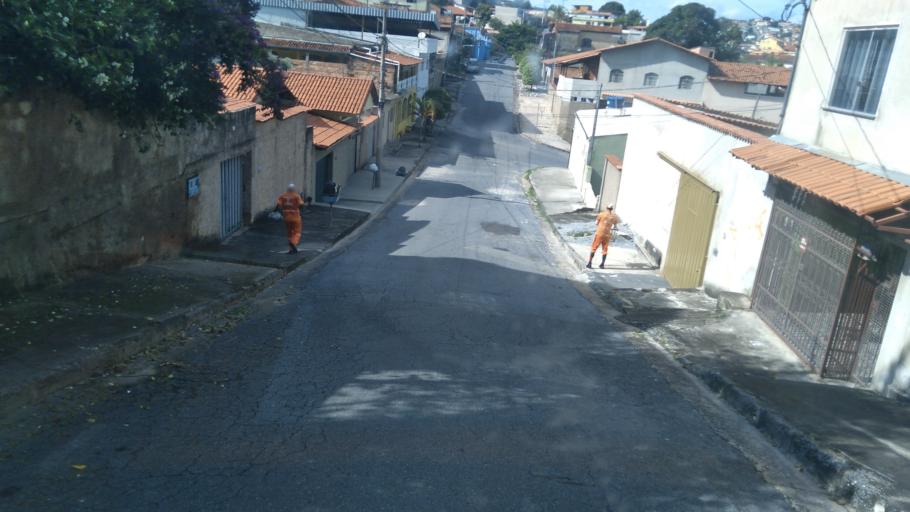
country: BR
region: Minas Gerais
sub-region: Belo Horizonte
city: Belo Horizonte
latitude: -19.8612
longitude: -43.9011
